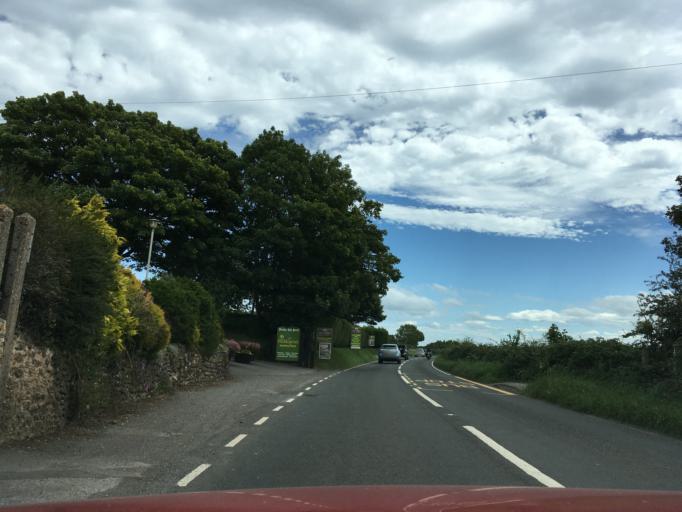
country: GB
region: England
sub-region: Somerset
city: Bradley Cross
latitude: 51.2432
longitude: -2.7326
